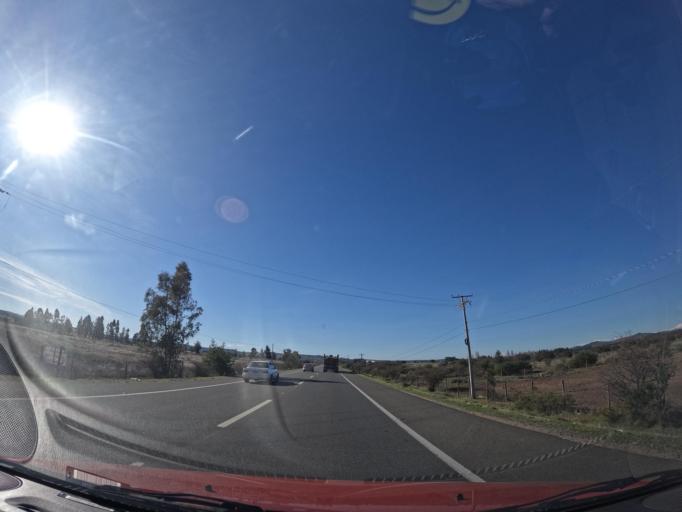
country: CL
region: Maule
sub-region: Provincia de Cauquenes
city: Cauquenes
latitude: -35.9582
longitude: -72.2153
